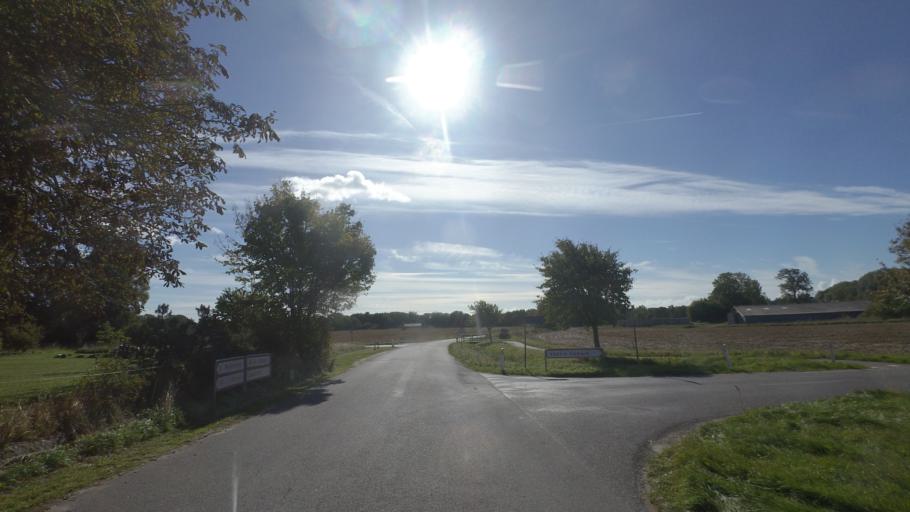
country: DK
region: Capital Region
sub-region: Bornholm Kommune
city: Akirkeby
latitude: 55.0097
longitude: 14.9919
